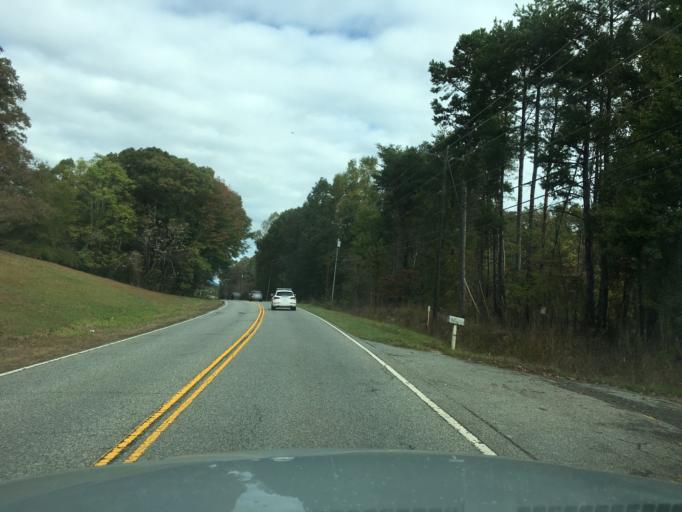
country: US
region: South Carolina
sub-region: Greenville County
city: Greer
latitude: 35.0335
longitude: -82.2655
